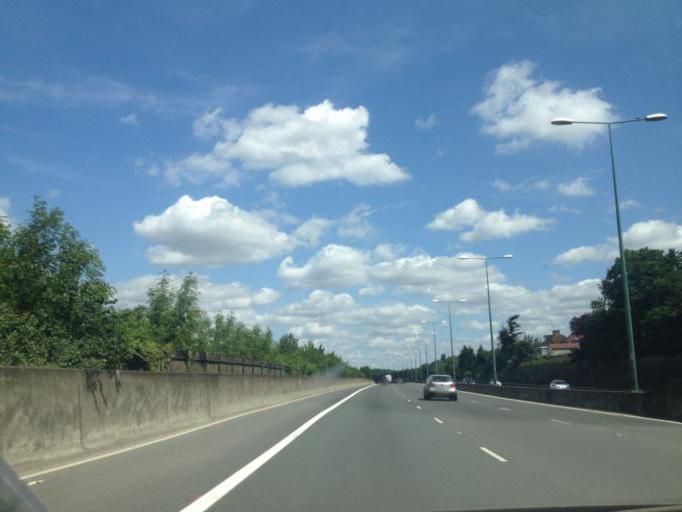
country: GB
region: England
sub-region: Greater London
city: Hendon
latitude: 51.5881
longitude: -0.2379
